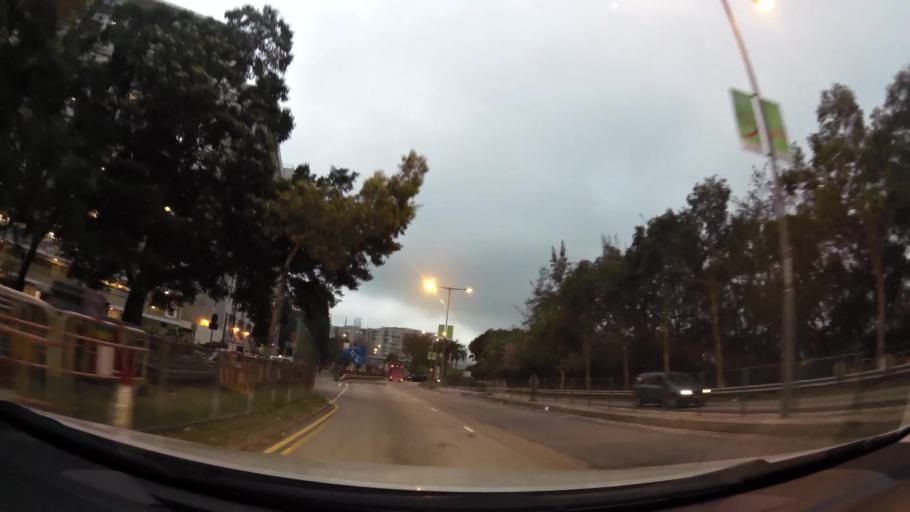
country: HK
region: Tsuen Wan
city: Tsuen Wan
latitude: 22.3457
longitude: 114.1101
